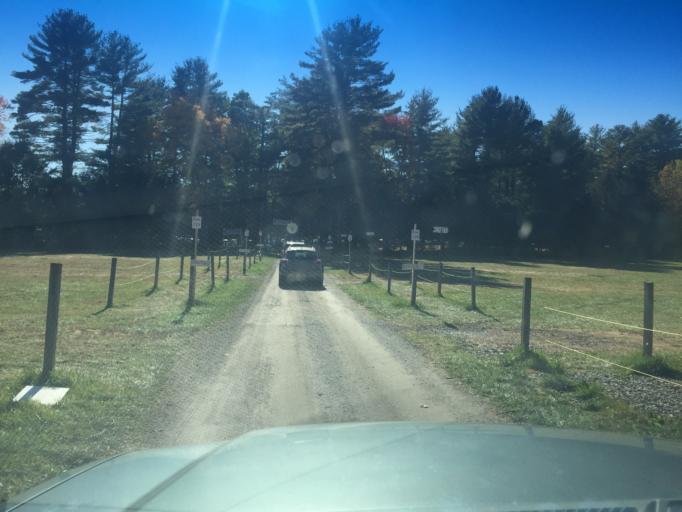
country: US
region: Massachusetts
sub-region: Middlesex County
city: Stow
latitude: 42.4107
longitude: -71.5178
